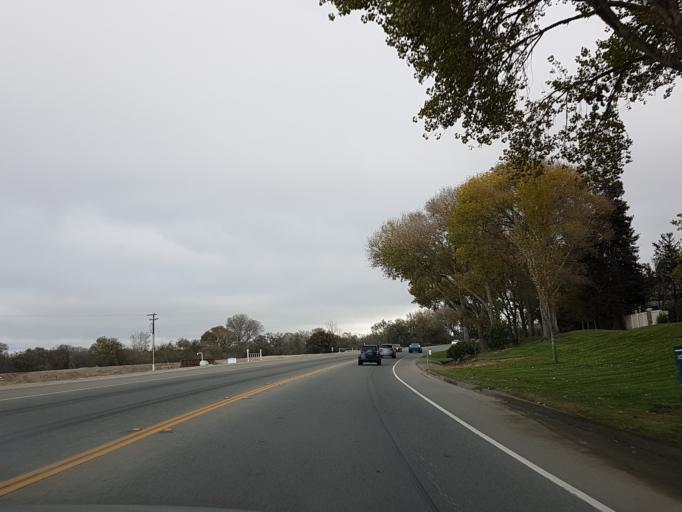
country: US
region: California
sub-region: Monterey County
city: Salinas
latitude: 36.6219
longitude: -121.6656
